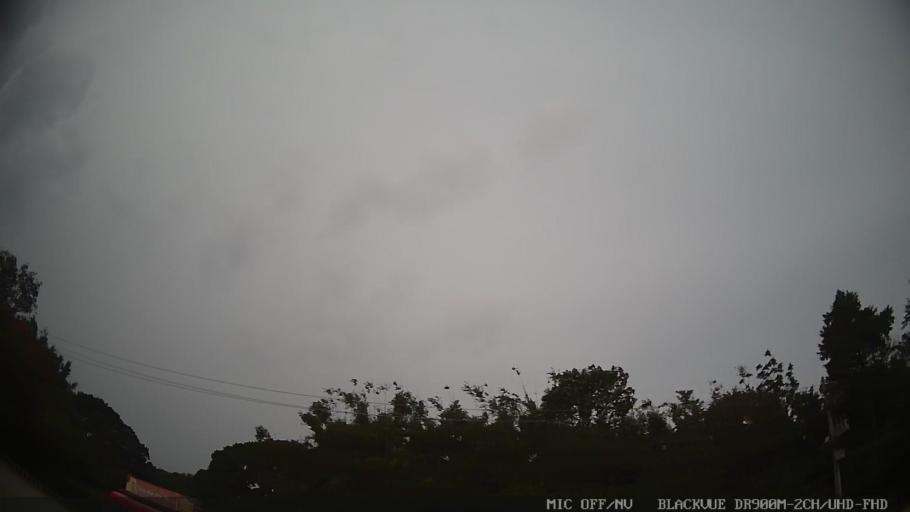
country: BR
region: Sao Paulo
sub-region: Braganca Paulista
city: Braganca Paulista
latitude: -22.9453
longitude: -46.6511
